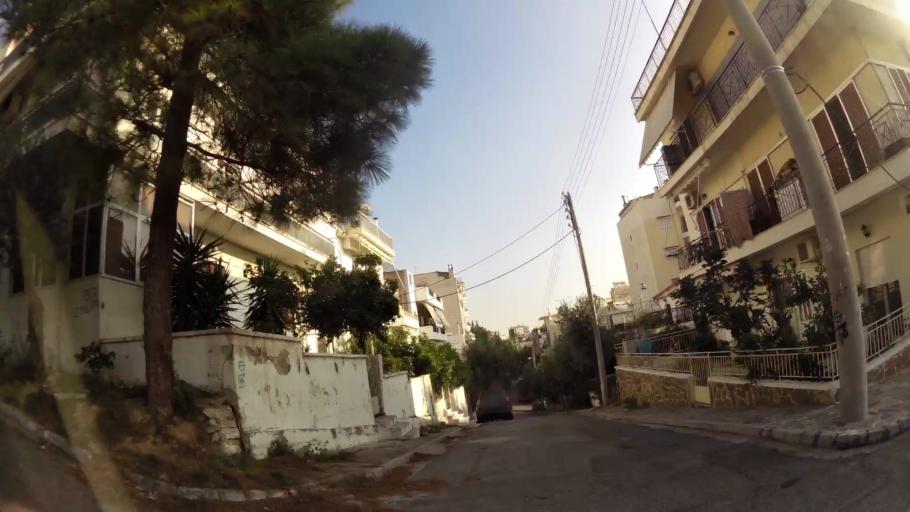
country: GR
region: Attica
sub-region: Nomos Piraios
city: Nikaia
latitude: 37.9706
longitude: 23.6356
